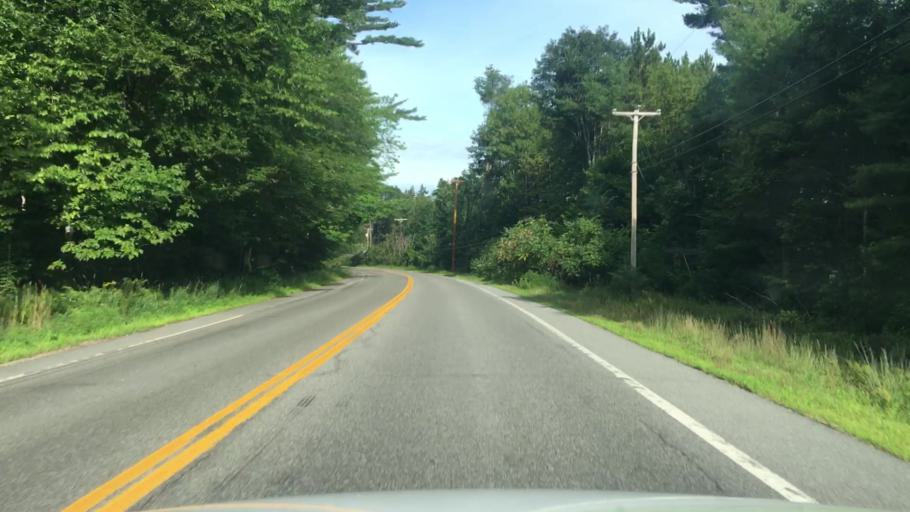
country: US
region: Maine
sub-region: York County
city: Cornish
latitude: 43.8057
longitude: -70.8361
